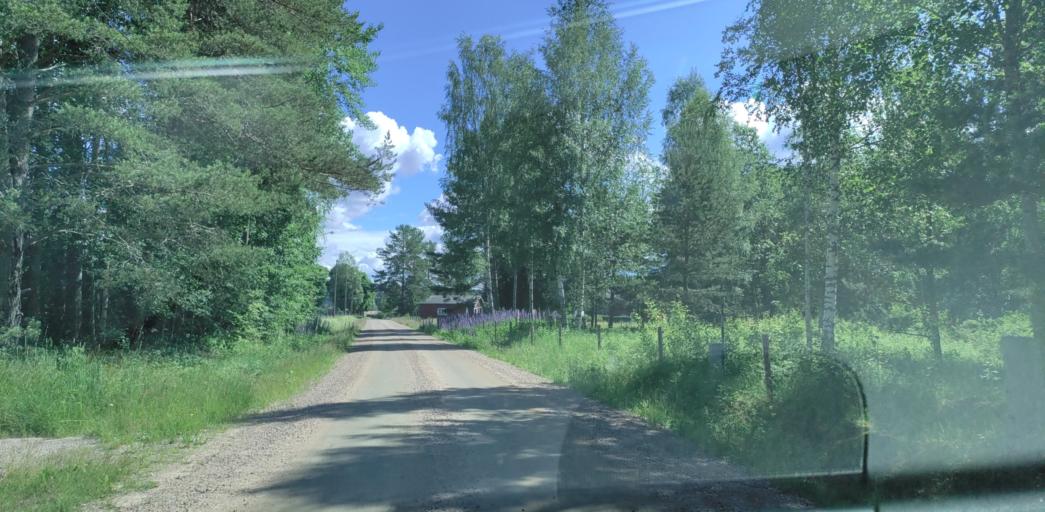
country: SE
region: Vaermland
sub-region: Munkfors Kommun
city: Munkfors
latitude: 59.9546
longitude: 13.4900
